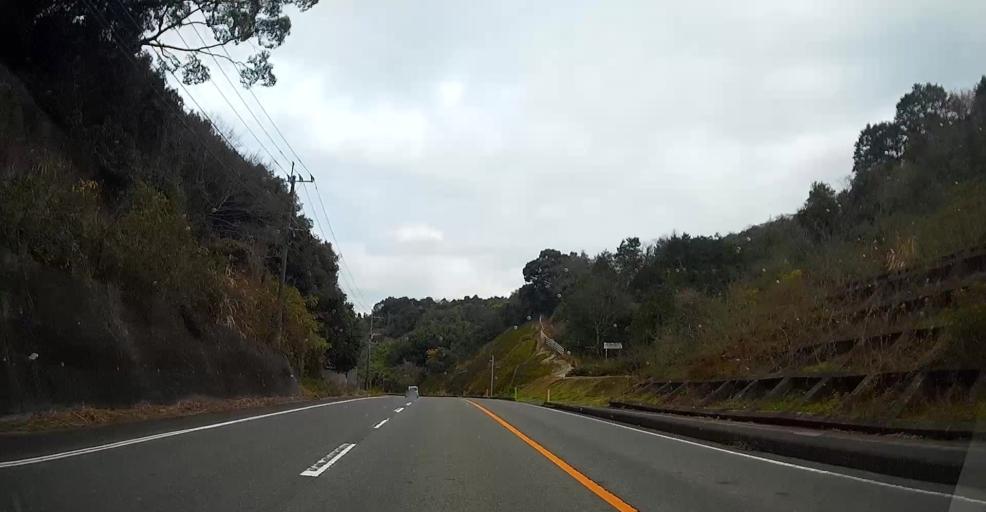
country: JP
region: Kumamoto
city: Hondo
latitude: 32.4945
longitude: 130.2979
